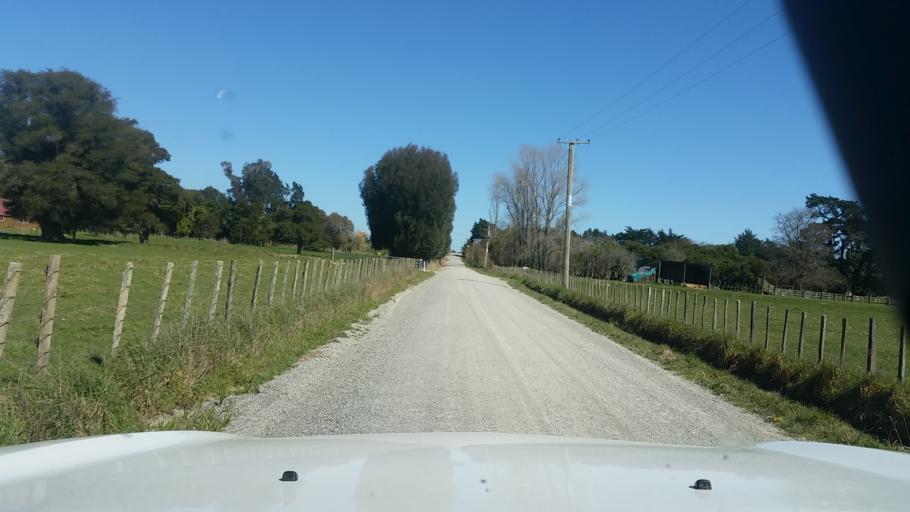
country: NZ
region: Wellington
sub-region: Masterton District
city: Masterton
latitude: -40.9877
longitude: 175.6206
